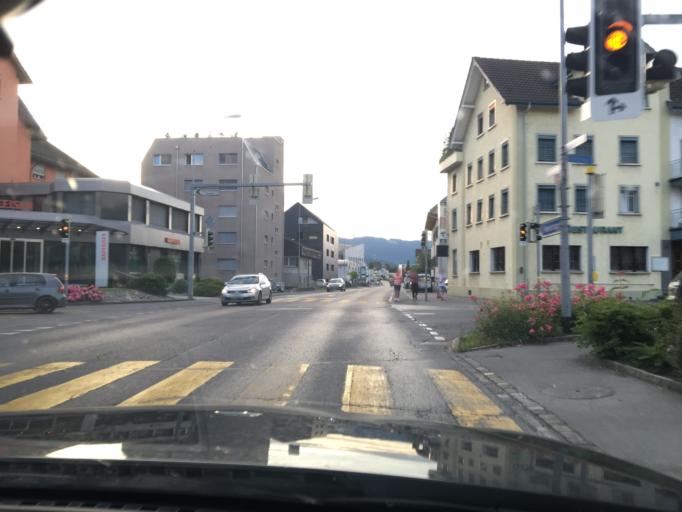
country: CH
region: Saint Gallen
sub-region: Wahlkreis Rheintal
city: Diepoldsau
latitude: 47.3859
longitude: 9.6549
